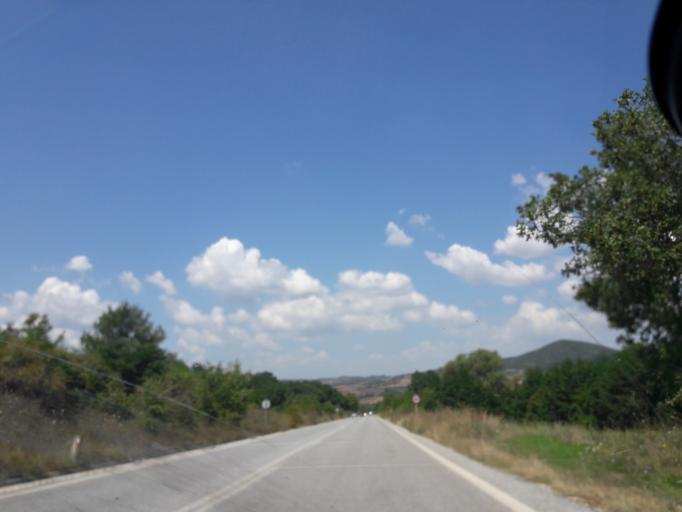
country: GR
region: Central Macedonia
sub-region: Nomos Chalkidikis
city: Polygyros
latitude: 40.4567
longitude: 23.4047
